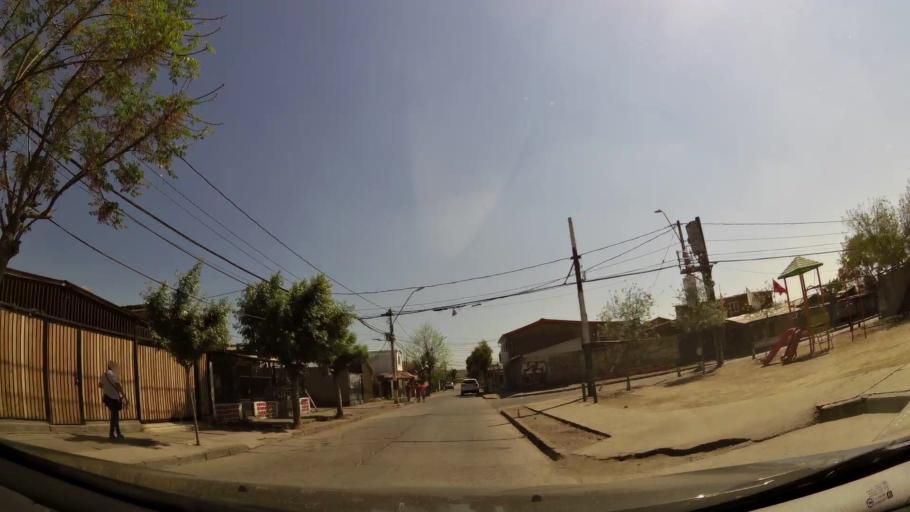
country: CL
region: Santiago Metropolitan
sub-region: Provincia de Maipo
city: San Bernardo
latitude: -33.5791
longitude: -70.7046
